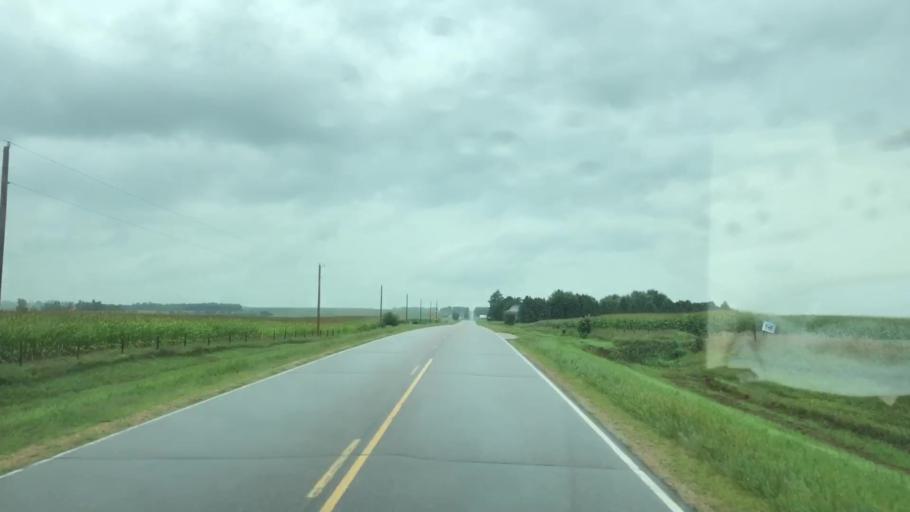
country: US
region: Iowa
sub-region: O'Brien County
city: Sanborn
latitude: 43.2536
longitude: -95.7235
